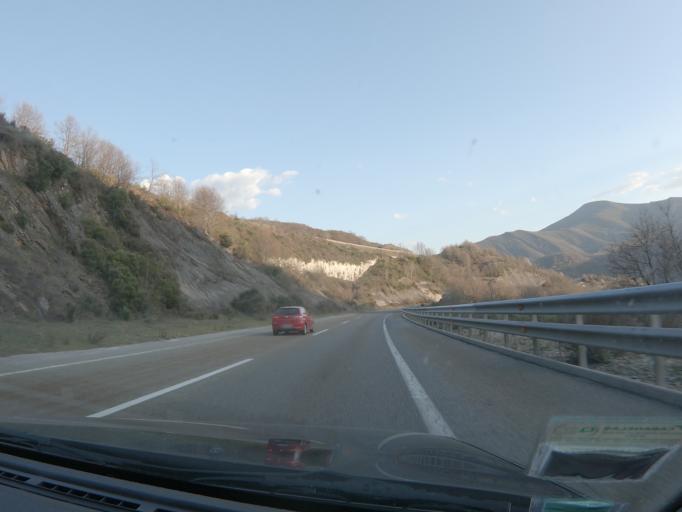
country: ES
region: Castille and Leon
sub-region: Provincia de Leon
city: Vega de Valcarce
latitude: 42.6868
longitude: -6.9888
